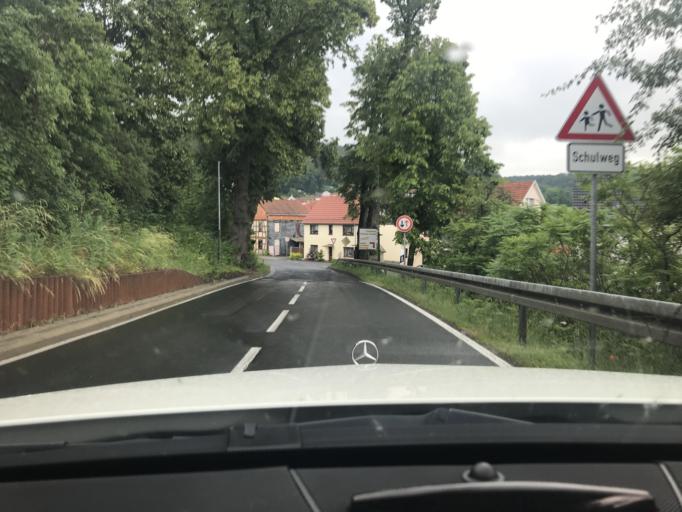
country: DE
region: Thuringia
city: Heyerode
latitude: 51.1645
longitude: 10.3170
